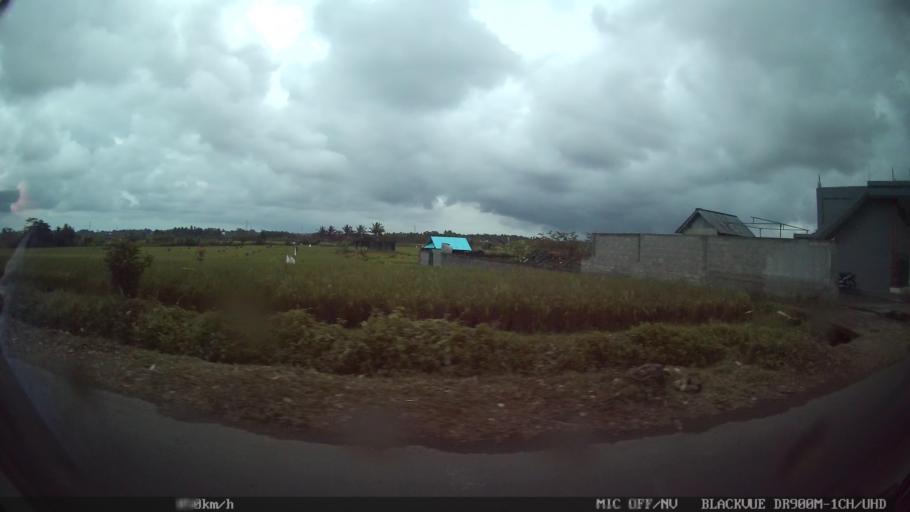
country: ID
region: Bali
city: Banjar Cemenggon
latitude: -8.5347
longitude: 115.1885
